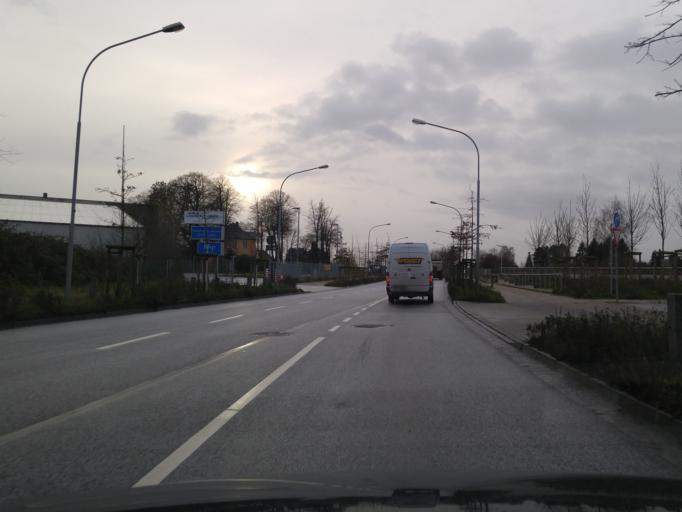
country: DE
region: Schleswig-Holstein
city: Luebeck
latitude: 53.8827
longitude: 10.6880
